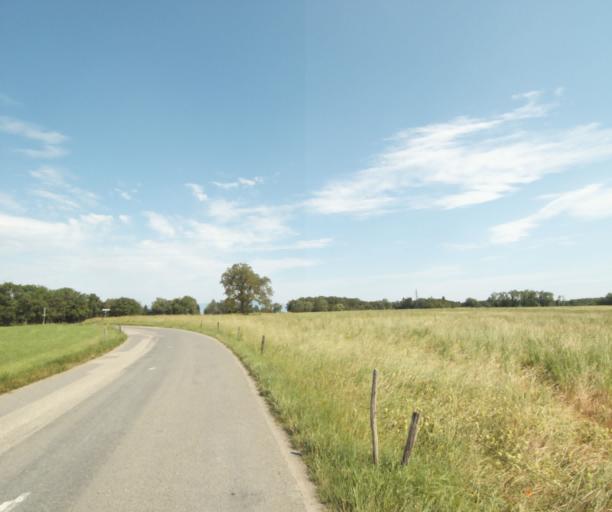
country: FR
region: Rhone-Alpes
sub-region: Departement de la Haute-Savoie
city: Allinges
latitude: 46.3275
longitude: 6.4948
